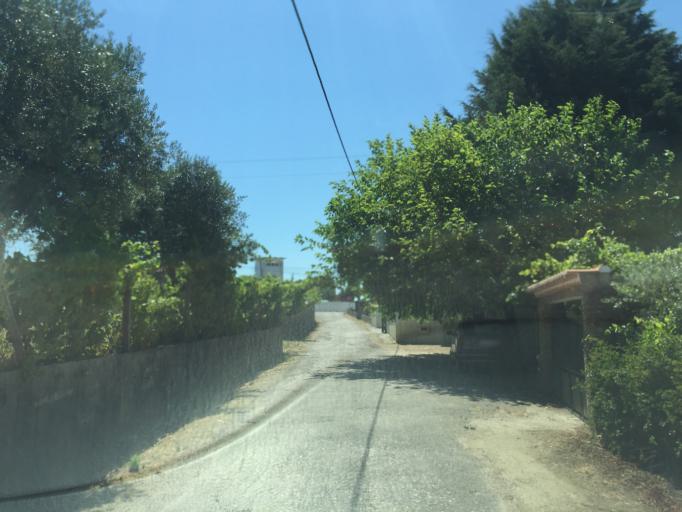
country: PT
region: Santarem
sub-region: Ferreira do Zezere
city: Ferreira do Zezere
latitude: 39.6199
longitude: -8.3122
